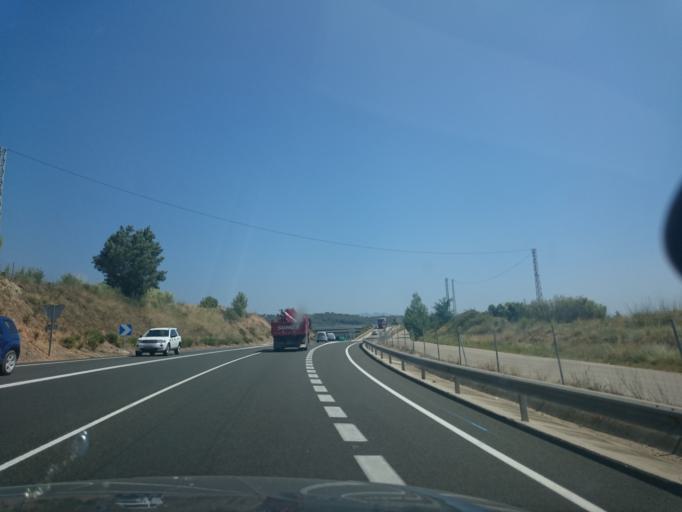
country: ES
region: Catalonia
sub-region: Provincia de Barcelona
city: Sant Pere de Riudebitlles
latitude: 41.4486
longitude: 1.6830
